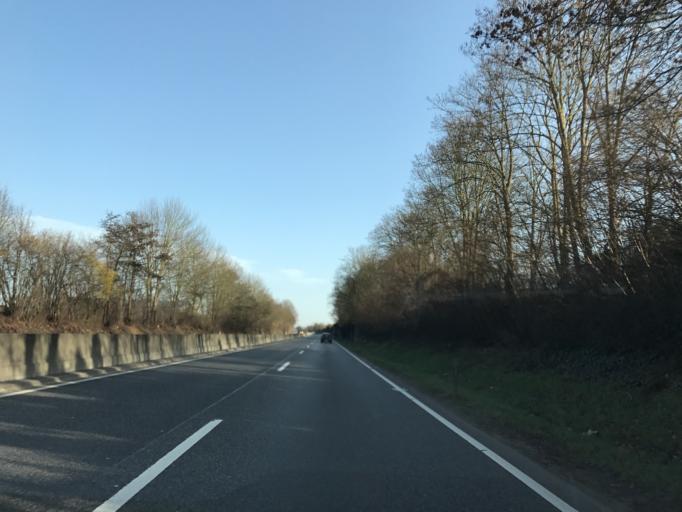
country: DE
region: Rheinland-Pfalz
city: Urmitz
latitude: 50.4387
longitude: 7.5112
